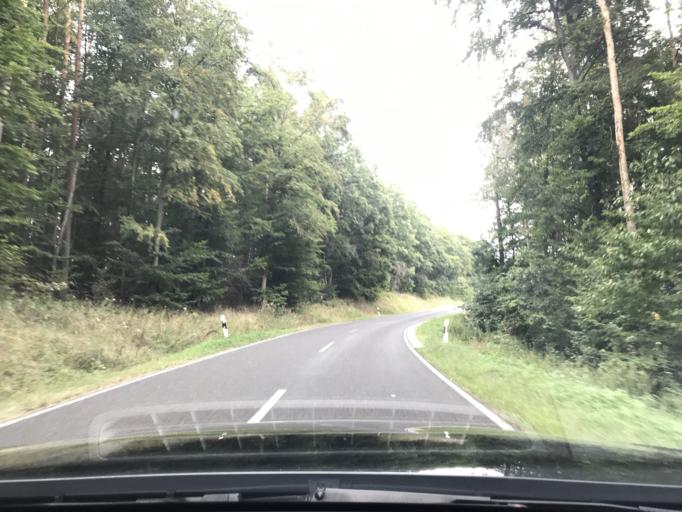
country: DE
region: Bavaria
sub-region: Regierungsbezirk Unterfranken
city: Breitbrunn
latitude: 50.0514
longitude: 10.6637
